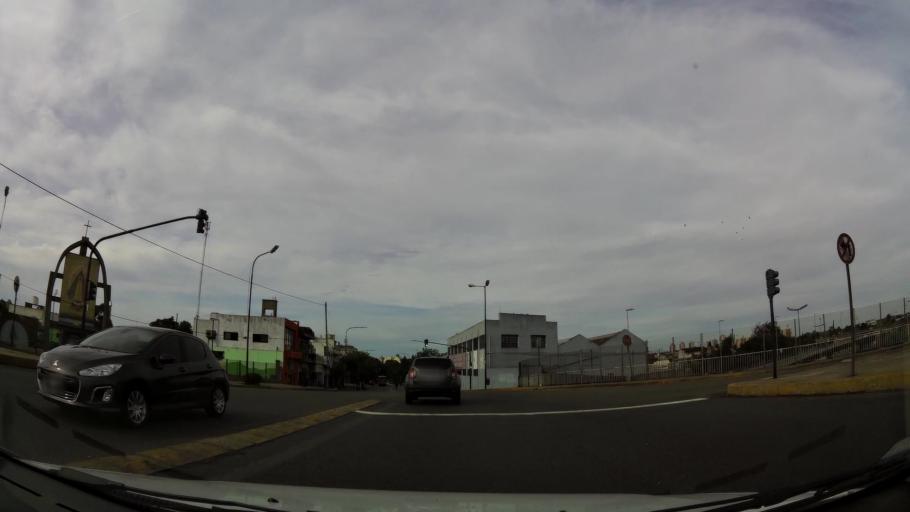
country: AR
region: Buenos Aires F.D.
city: Villa Lugano
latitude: -34.6495
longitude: -58.4696
